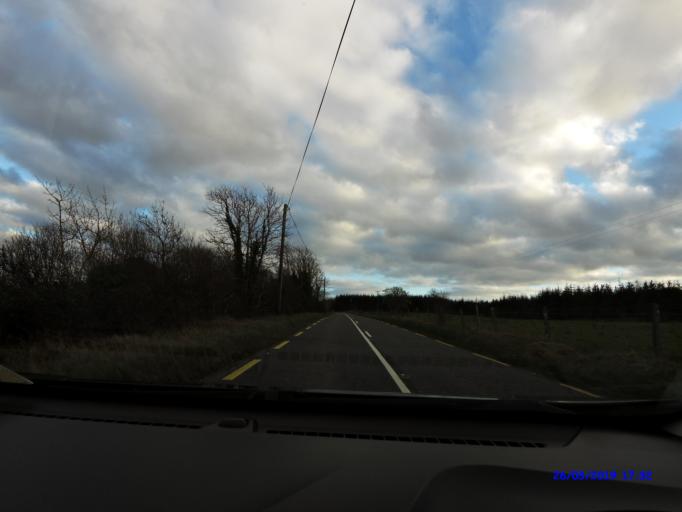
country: IE
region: Connaught
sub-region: Maigh Eo
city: Ballyhaunis
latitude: 53.6743
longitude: -8.7447
